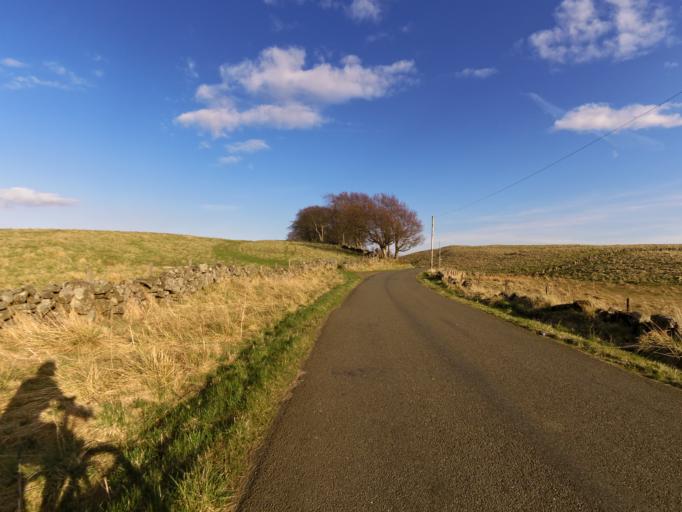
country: GB
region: Scotland
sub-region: Fife
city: Falkland
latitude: 56.2351
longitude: -3.2402
